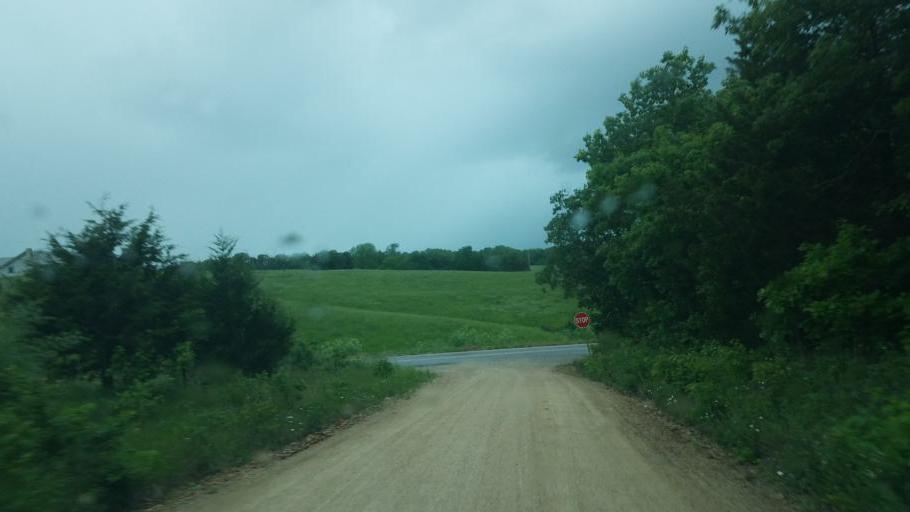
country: US
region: Missouri
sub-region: Moniteau County
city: California
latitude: 38.7469
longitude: -92.6459
